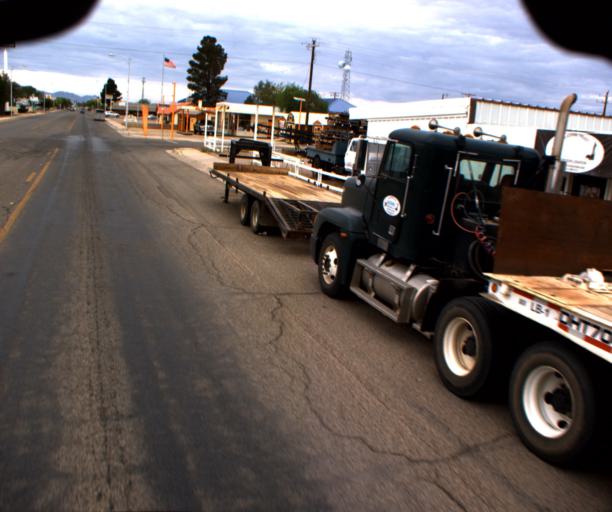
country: US
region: Arizona
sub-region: Cochise County
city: Willcox
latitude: 32.2567
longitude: -109.8297
